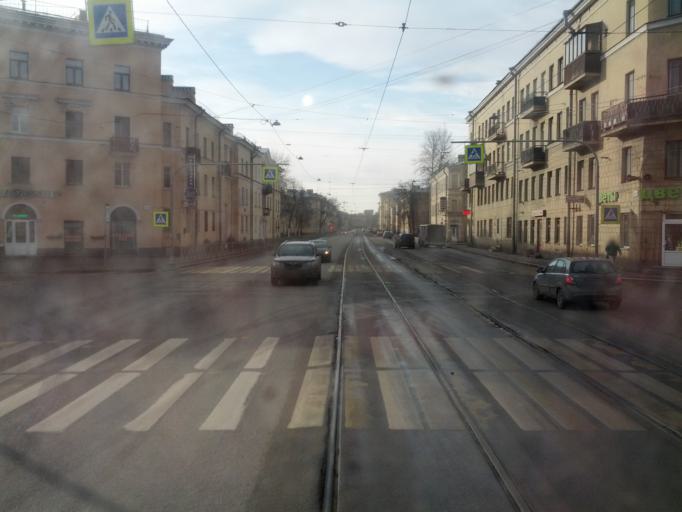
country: RU
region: Leningrad
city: Kalininskiy
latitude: 59.9523
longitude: 30.4149
